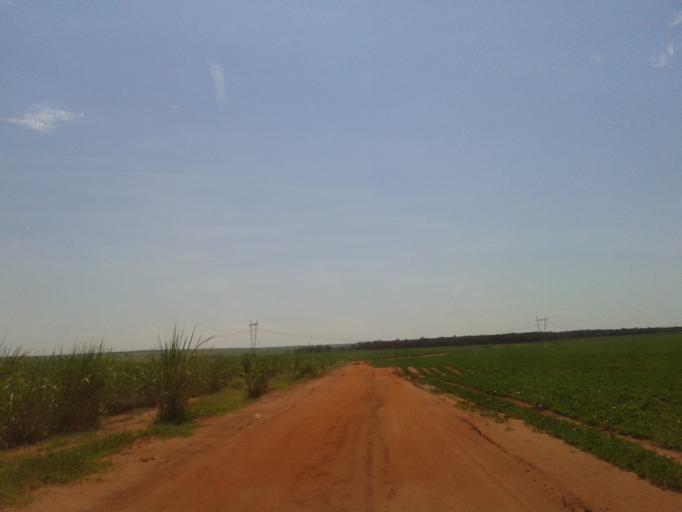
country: BR
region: Minas Gerais
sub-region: Santa Vitoria
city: Santa Vitoria
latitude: -19.0644
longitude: -50.4736
